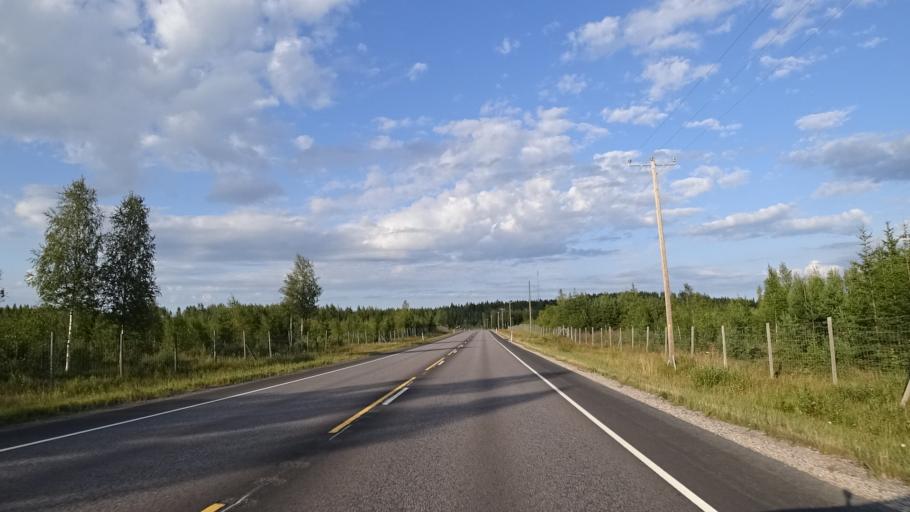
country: FI
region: South Karelia
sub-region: Imatra
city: Rautjaervi
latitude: 61.3610
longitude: 29.2108
